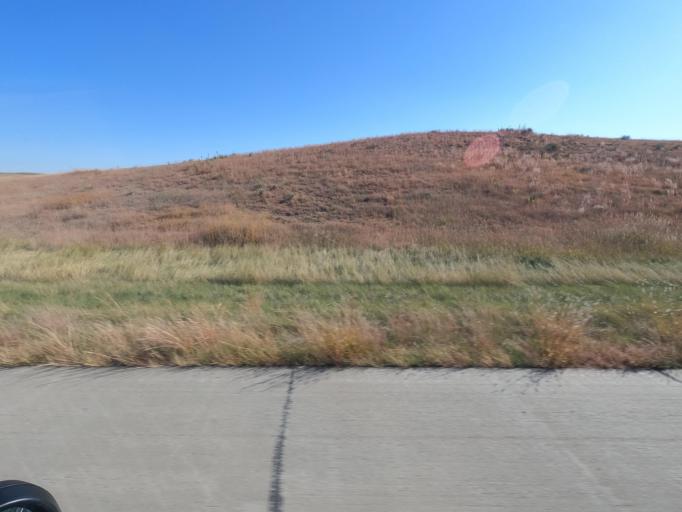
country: US
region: Colorado
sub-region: Sedgwick County
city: Julesburg
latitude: 40.9263
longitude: -102.3406
